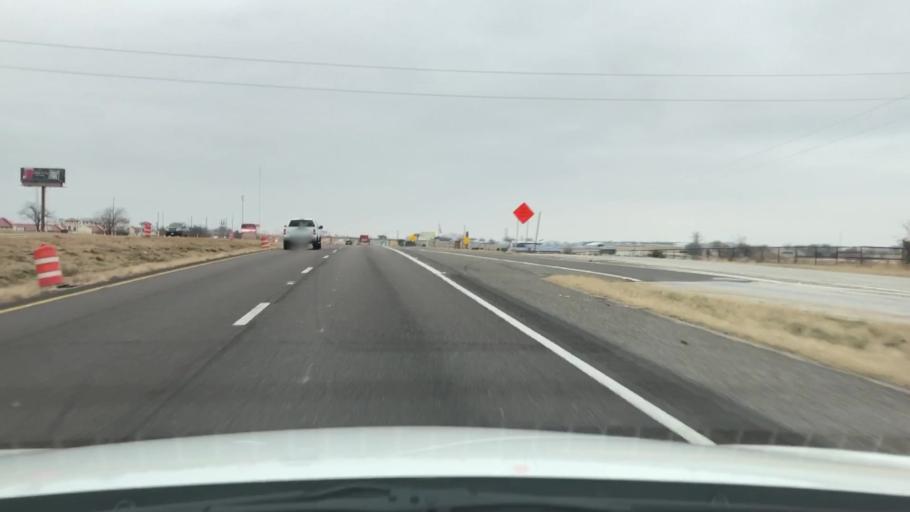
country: US
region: Texas
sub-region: Cooke County
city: Gainesville
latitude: 33.6751
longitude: -97.1524
